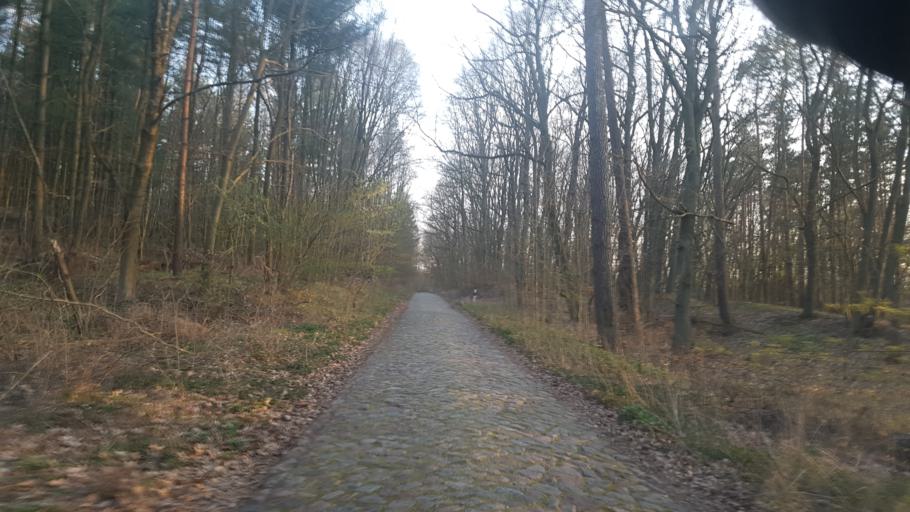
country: DE
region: Brandenburg
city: Gramzow
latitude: 53.2089
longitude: 13.9365
